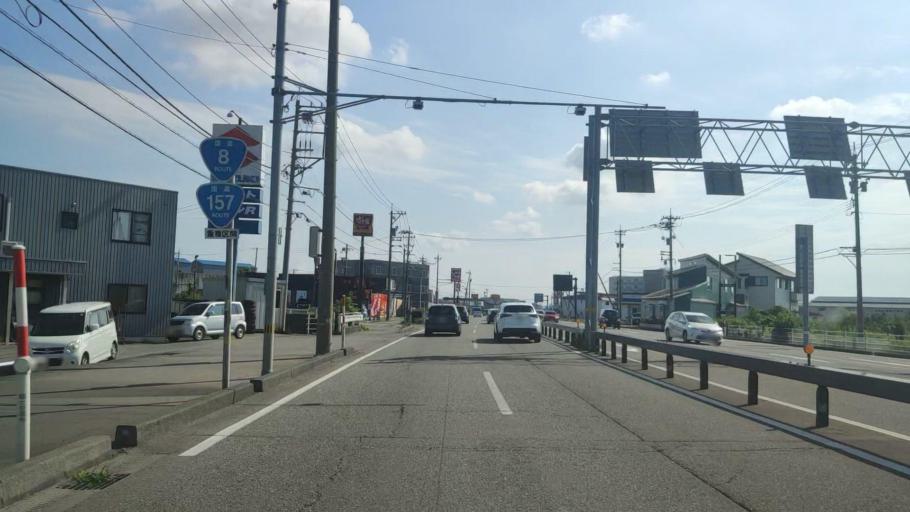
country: JP
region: Ishikawa
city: Matsuto
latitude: 36.5247
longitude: 136.5837
